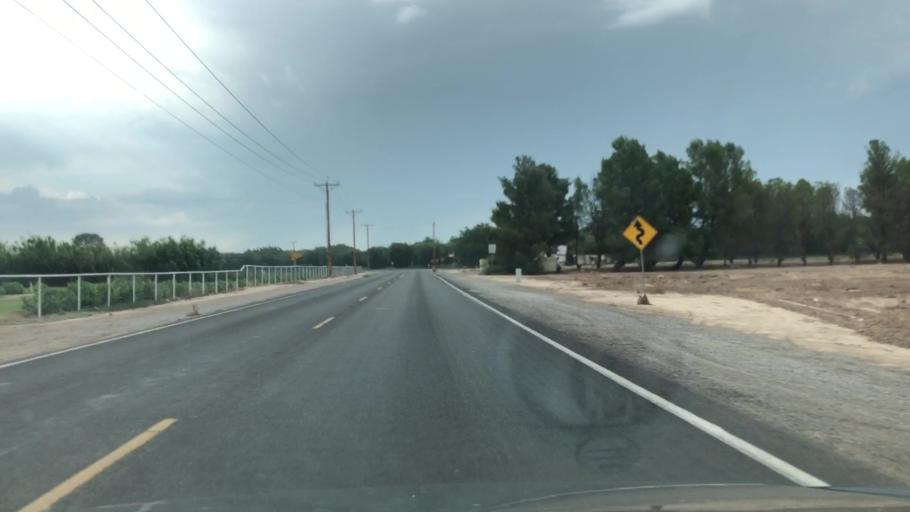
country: US
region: Texas
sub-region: El Paso County
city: Vinton
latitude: 31.9306
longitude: -106.6294
